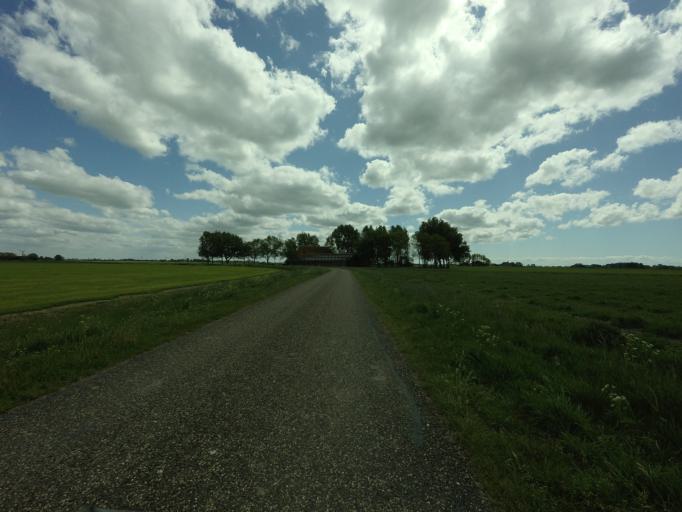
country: NL
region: Friesland
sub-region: Gemeente Franekeradeel
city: Tzum
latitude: 53.1377
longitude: 5.5578
